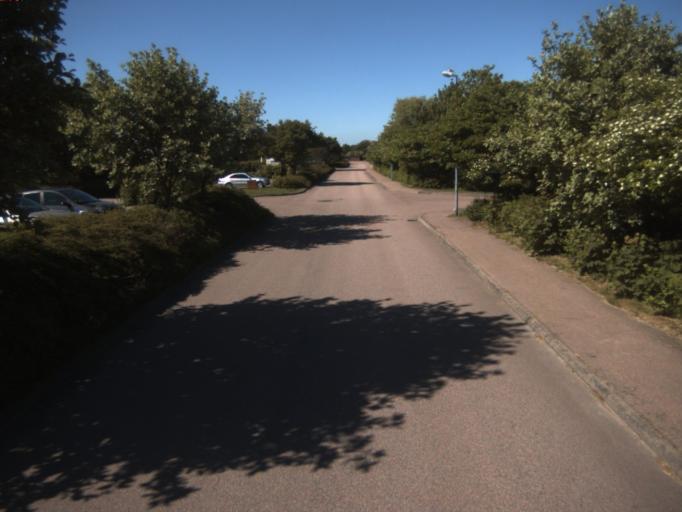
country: SE
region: Skane
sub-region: Helsingborg
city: Rydeback
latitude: 55.9594
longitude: 12.7722
